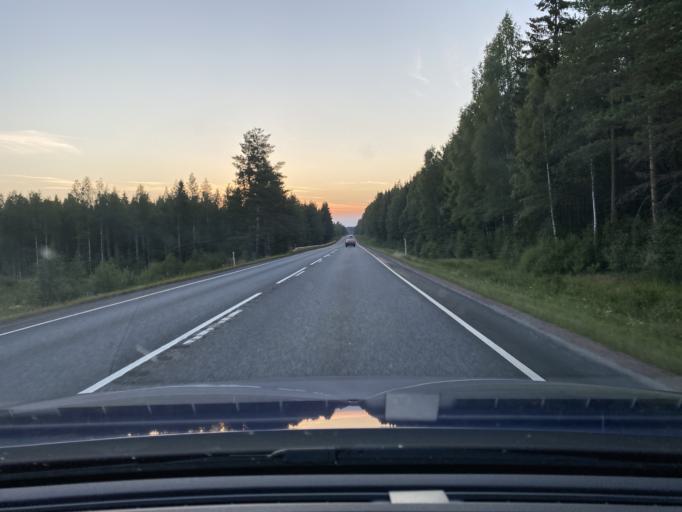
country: FI
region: Pirkanmaa
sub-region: Luoteis-Pirkanmaa
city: Ikaalinen
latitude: 61.7950
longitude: 22.9816
